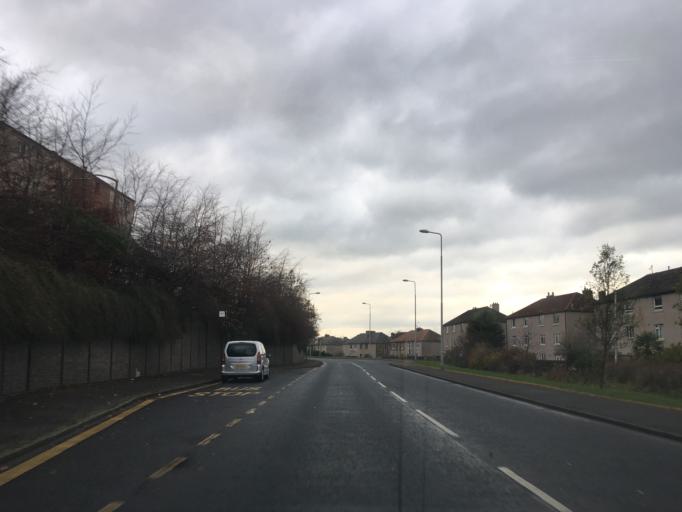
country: GB
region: Scotland
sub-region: Edinburgh
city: Colinton
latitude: 55.9203
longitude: -3.2805
